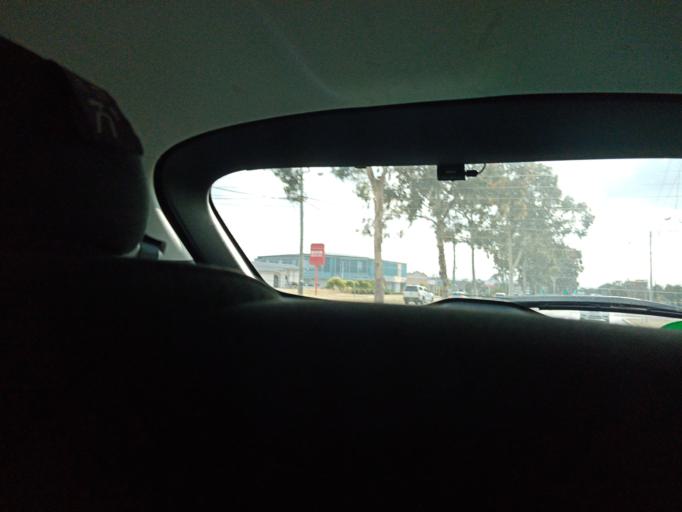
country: AU
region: Western Australia
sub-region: Canning
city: Wilson
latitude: -32.0131
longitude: 115.9227
